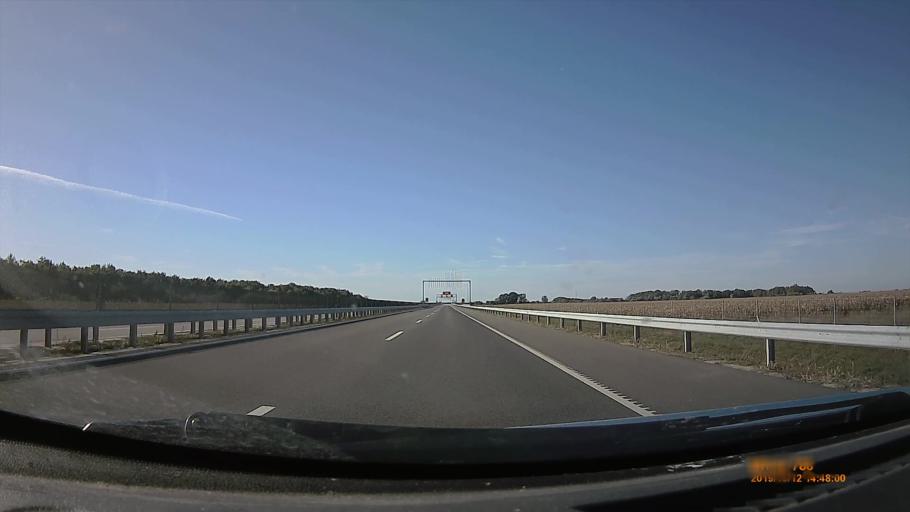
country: HU
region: Hajdu-Bihar
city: Berettyoujfalu
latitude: 47.2871
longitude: 21.5229
